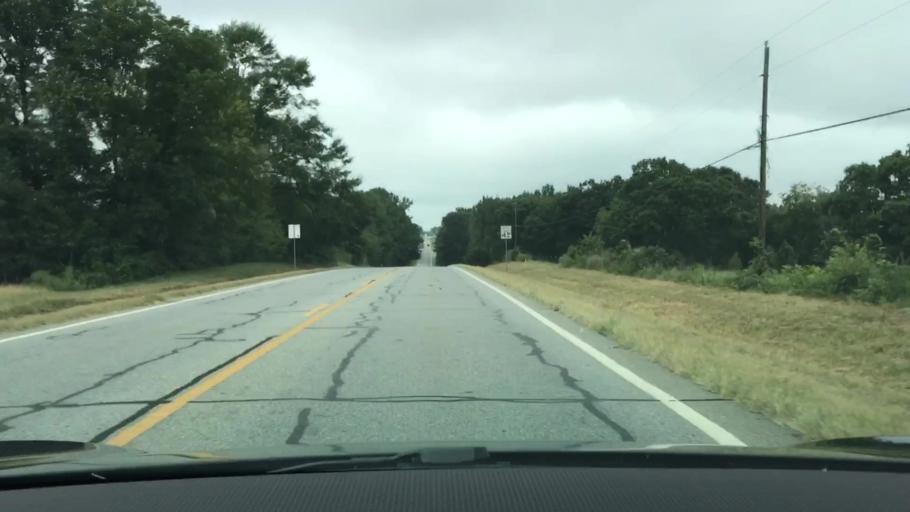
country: US
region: Georgia
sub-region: Oconee County
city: Watkinsville
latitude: 33.8474
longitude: -83.3925
